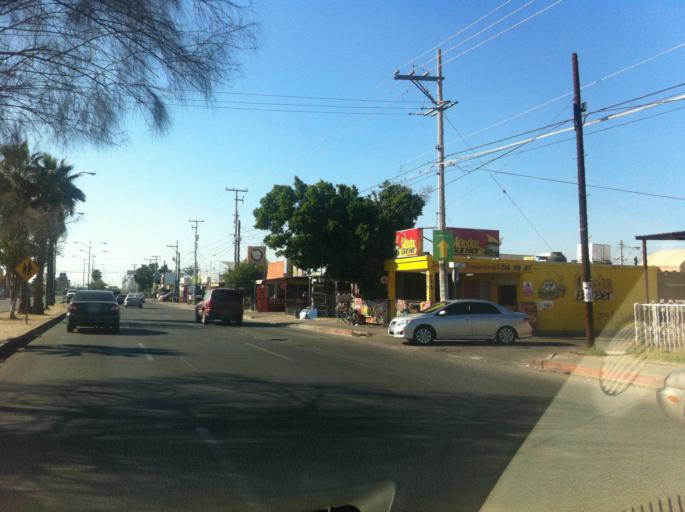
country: MX
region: Sonora
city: Hermosillo
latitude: 29.1161
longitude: -110.9924
